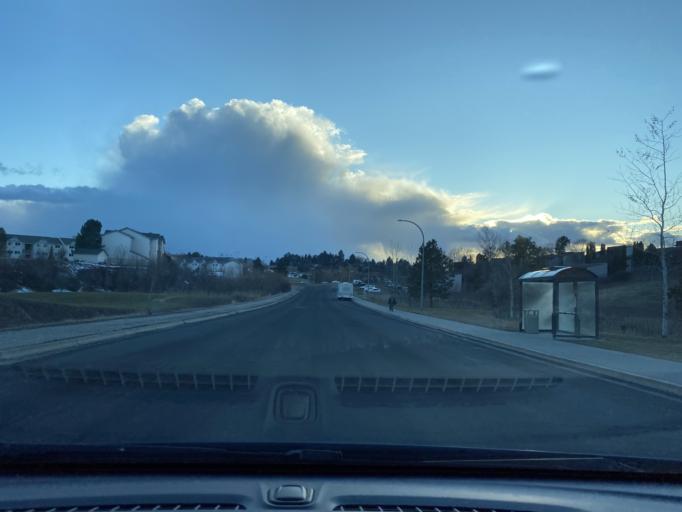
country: US
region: Washington
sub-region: Whitman County
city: Pullman
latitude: 46.7444
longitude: -117.1478
